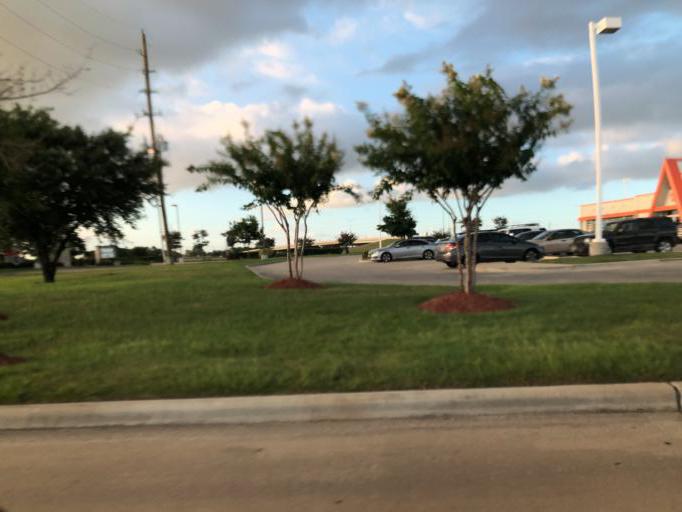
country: US
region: Texas
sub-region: Harris County
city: Katy
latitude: 29.7745
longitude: -95.8208
